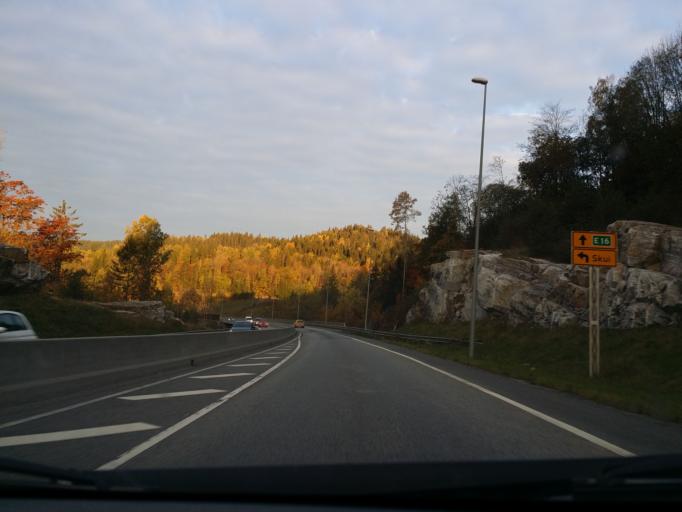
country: NO
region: Akershus
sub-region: Baerum
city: Skui
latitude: 59.9379
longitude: 10.4301
